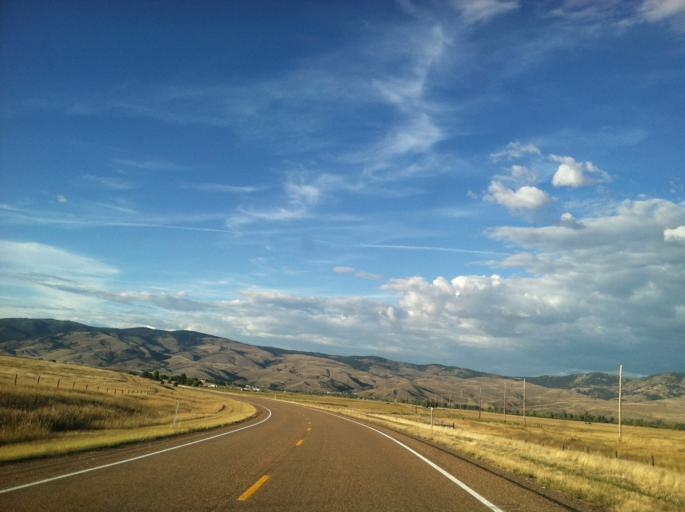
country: US
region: Montana
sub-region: Granite County
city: Philipsburg
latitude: 46.6247
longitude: -113.1704
